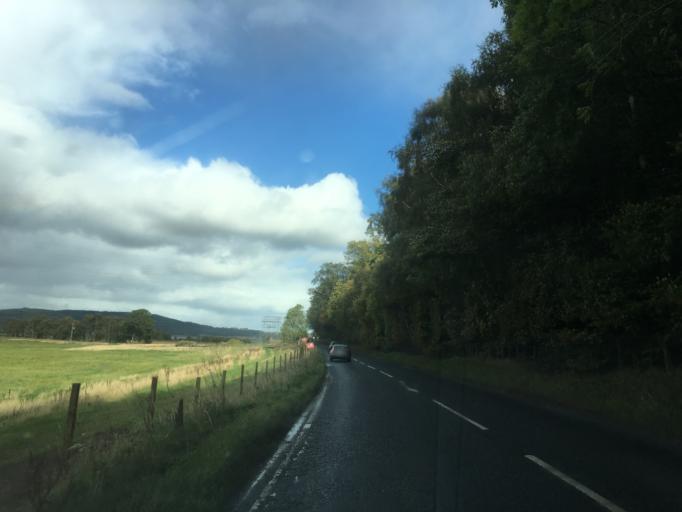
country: GB
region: Scotland
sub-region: Highland
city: Beauly
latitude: 57.4750
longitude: -4.3751
